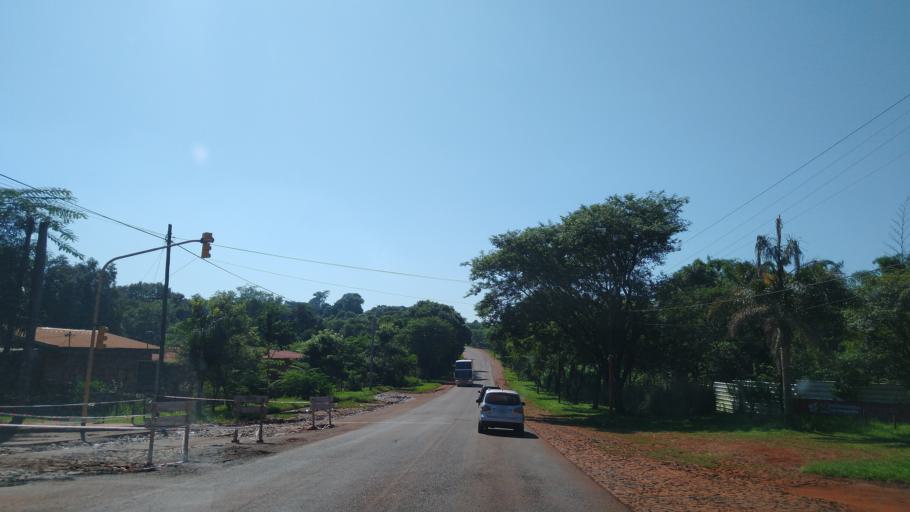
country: AR
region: Misiones
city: Puerto Esperanza
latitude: -26.0223
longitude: -54.6029
